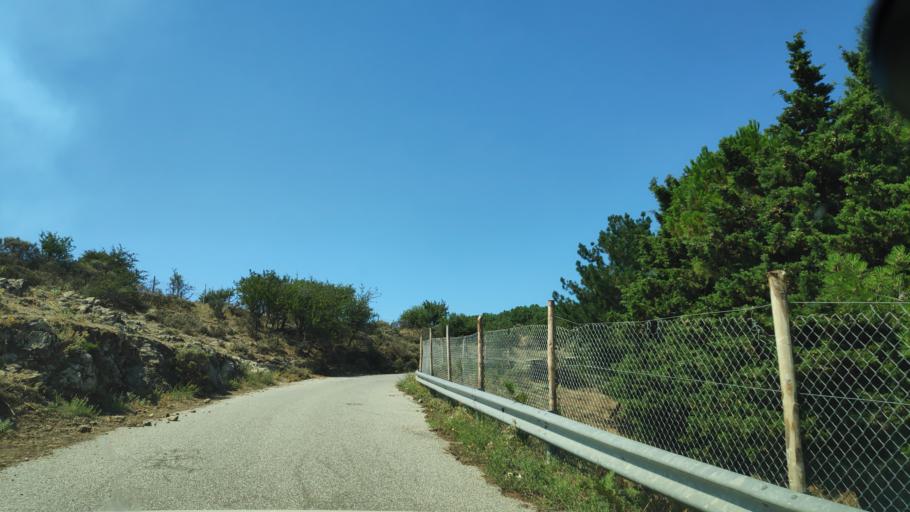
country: IT
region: Calabria
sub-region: Provincia di Reggio Calabria
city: Bova
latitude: 38.0135
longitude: 15.9352
